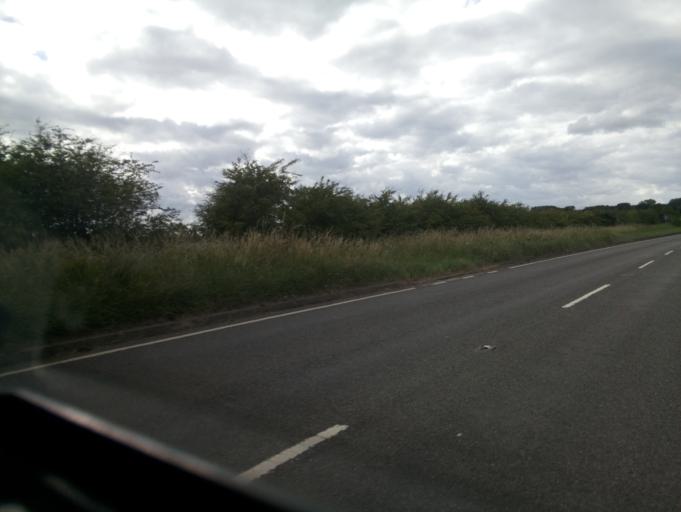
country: GB
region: England
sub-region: Leicestershire
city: Market Bosworth
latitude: 52.6216
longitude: -1.4808
